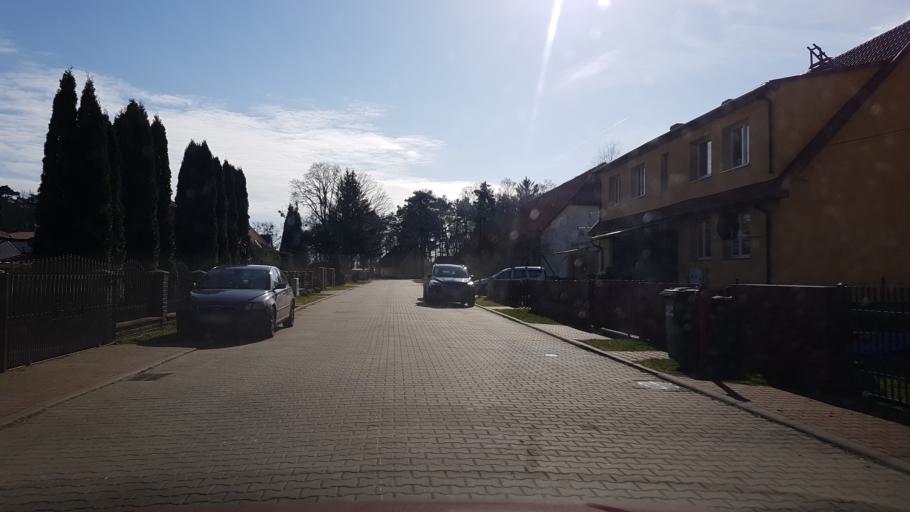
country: PL
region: West Pomeranian Voivodeship
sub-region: Powiat policki
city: Nowe Warpno
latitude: 53.7363
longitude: 14.3092
